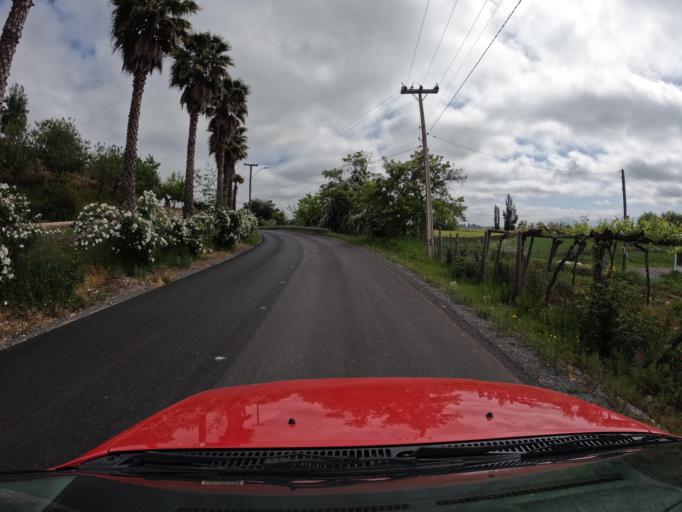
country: CL
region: O'Higgins
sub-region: Provincia de Colchagua
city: Santa Cruz
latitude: -34.6627
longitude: -71.3996
